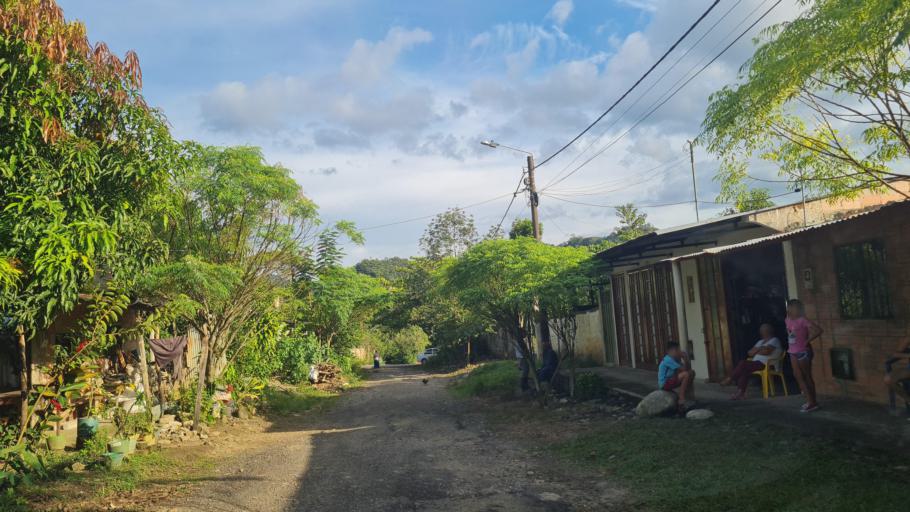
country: CO
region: Boyaca
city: San Luis de Gaceno
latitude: 4.8185
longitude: -73.1696
